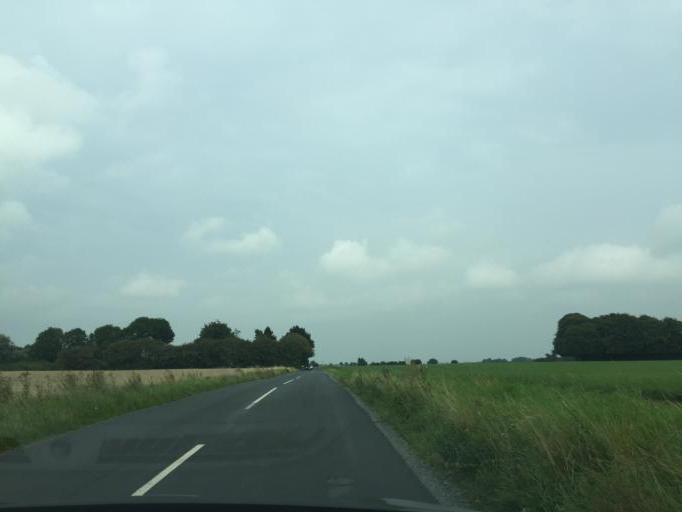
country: DK
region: South Denmark
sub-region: Odense Kommune
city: Hojby
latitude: 55.3188
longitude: 10.4224
